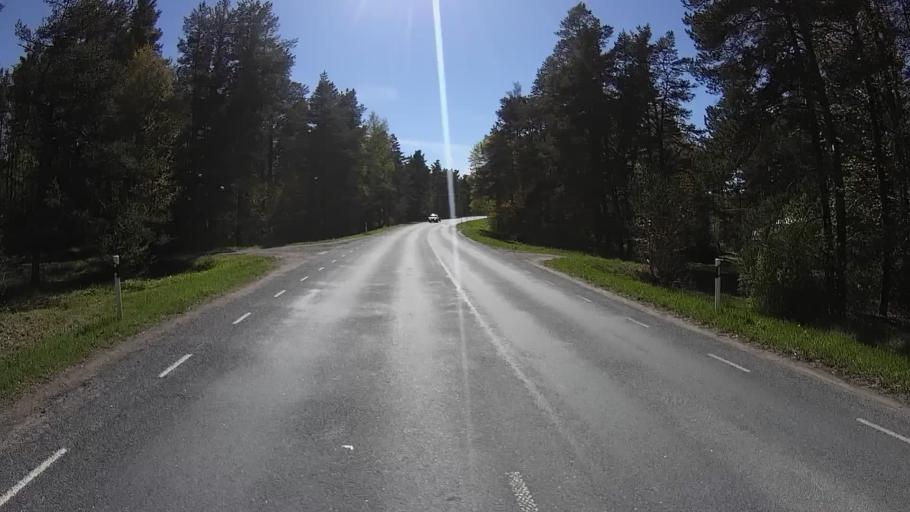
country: EE
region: Harju
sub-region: Loksa linn
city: Loksa
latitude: 59.5301
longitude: 25.7129
